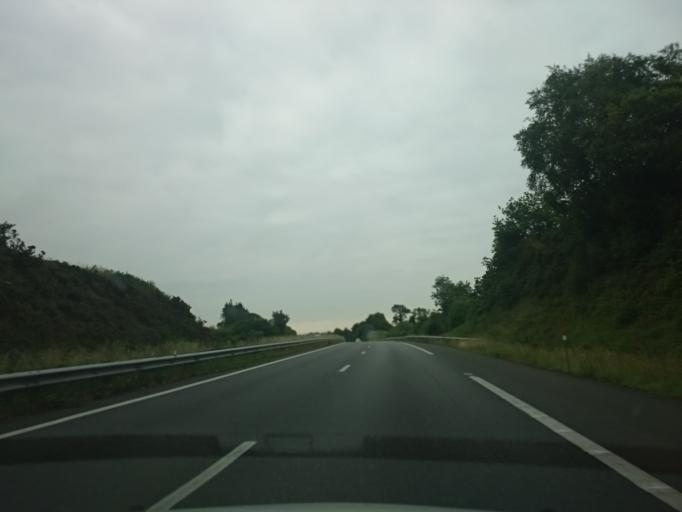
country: FR
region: Brittany
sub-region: Departement du Finistere
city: Hopital-Camfrout
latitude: 48.3197
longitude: -4.2210
